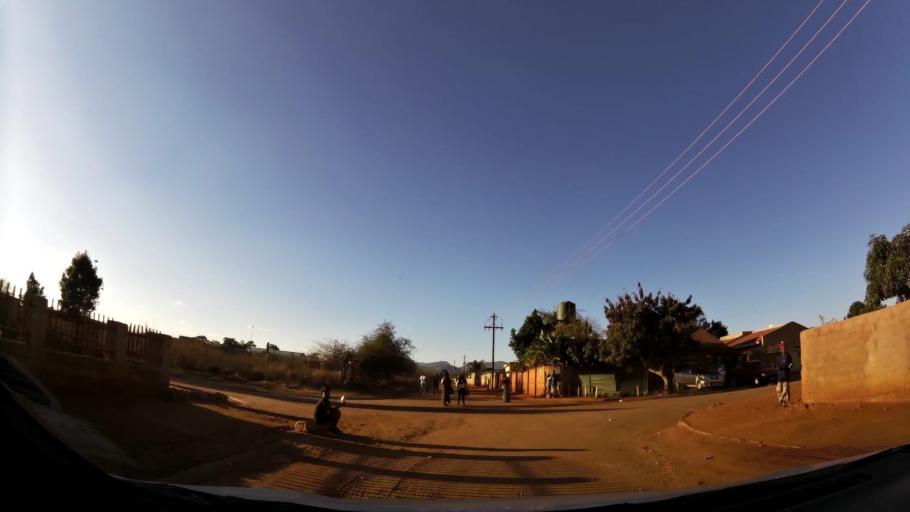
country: ZA
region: Limpopo
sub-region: Waterberg District Municipality
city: Mokopane
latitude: -24.1516
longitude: 28.9942
